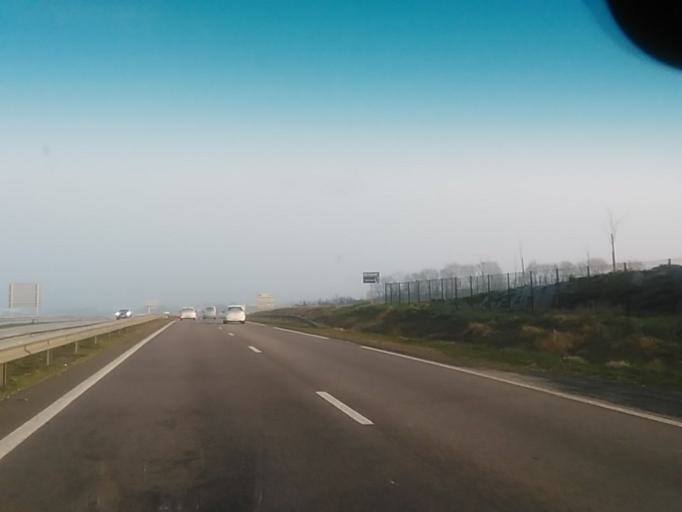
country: FR
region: Lower Normandy
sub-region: Departement du Calvados
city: Bourguebus
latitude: 49.0796
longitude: -0.3009
